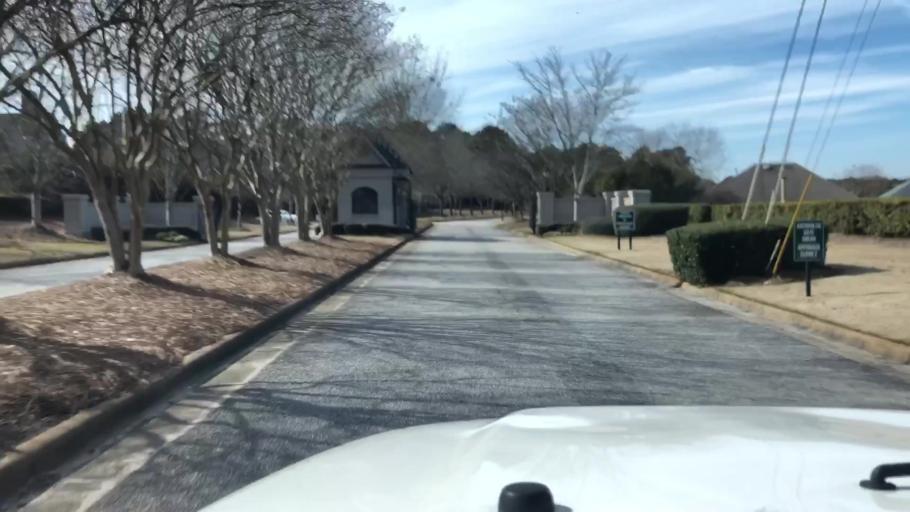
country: US
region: Alabama
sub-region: Montgomery County
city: Pike Road
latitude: 32.3595
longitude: -86.1438
